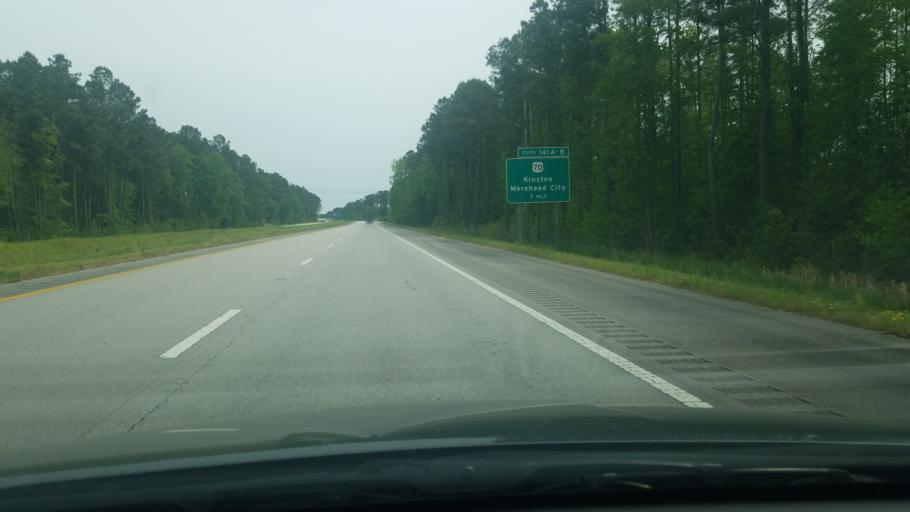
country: US
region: North Carolina
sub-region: Craven County
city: River Bend
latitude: 35.1176
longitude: -77.1577
